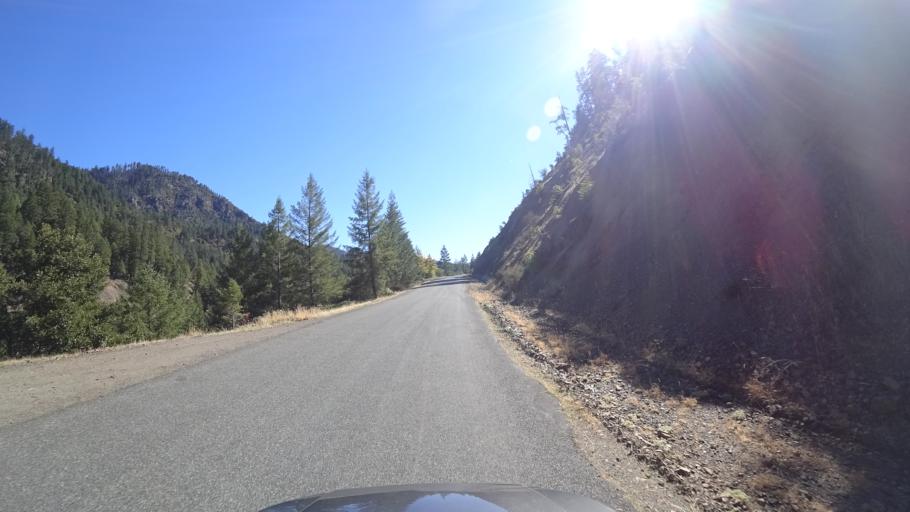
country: US
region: California
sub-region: Humboldt County
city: Willow Creek
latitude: 41.3126
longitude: -123.3782
